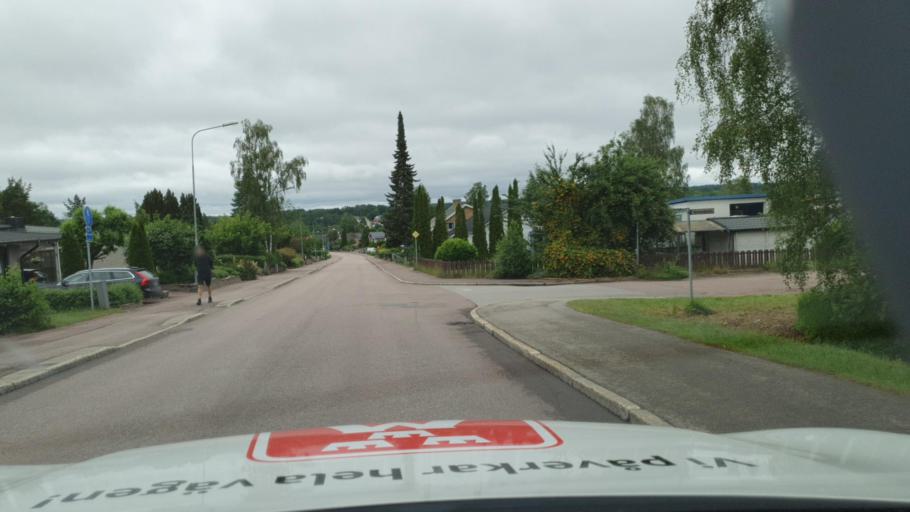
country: SE
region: Vaermland
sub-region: Grums Kommun
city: Grums
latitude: 59.3568
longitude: 13.1061
